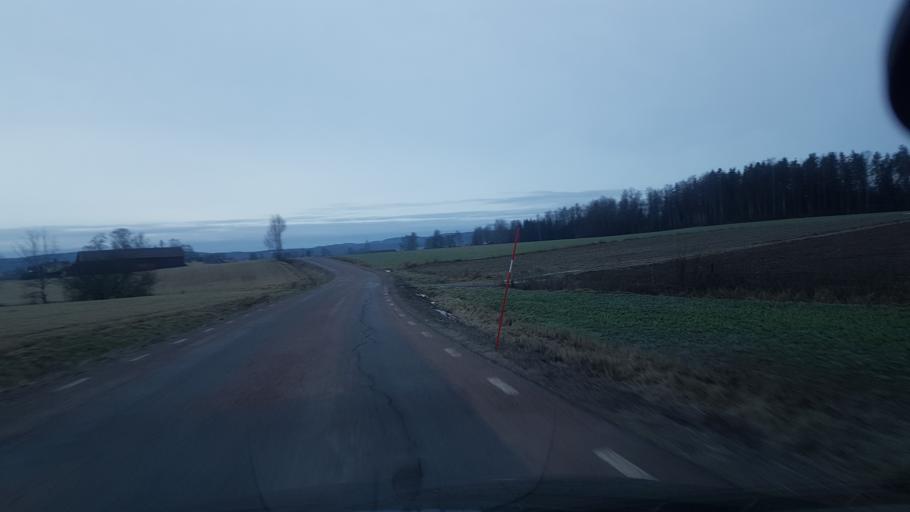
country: SE
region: Dalarna
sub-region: Saters Kommun
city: Saeter
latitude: 60.4333
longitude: 15.6563
